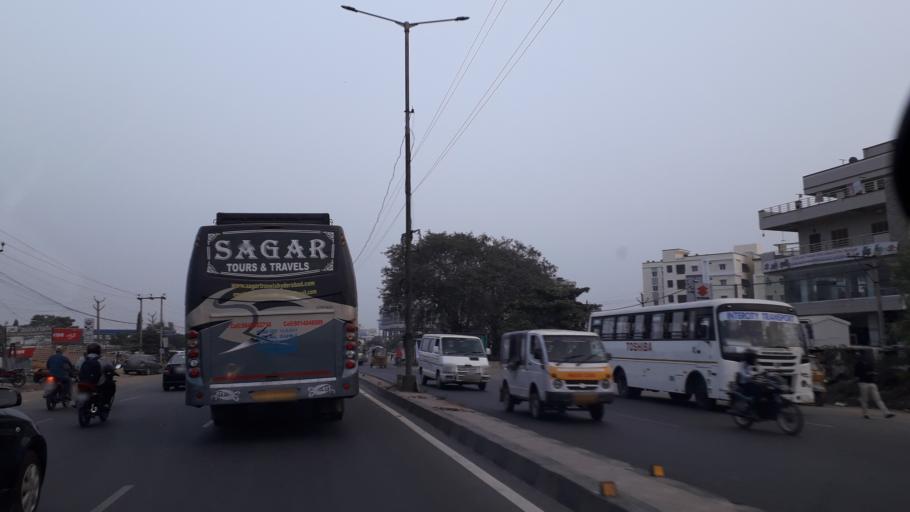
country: IN
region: Telangana
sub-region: Medak
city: Serilingampalle
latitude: 17.5126
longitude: 78.2915
